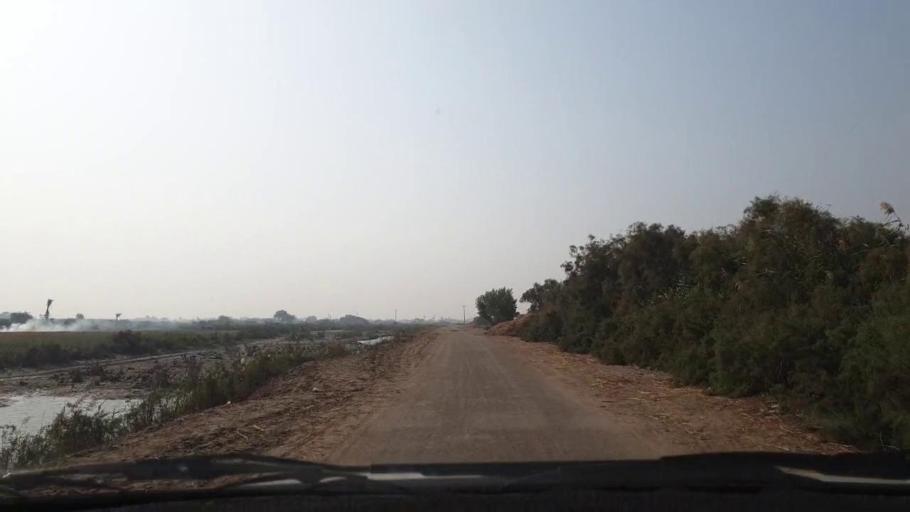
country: PK
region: Sindh
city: Tando Muhammad Khan
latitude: 25.0230
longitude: 68.4502
